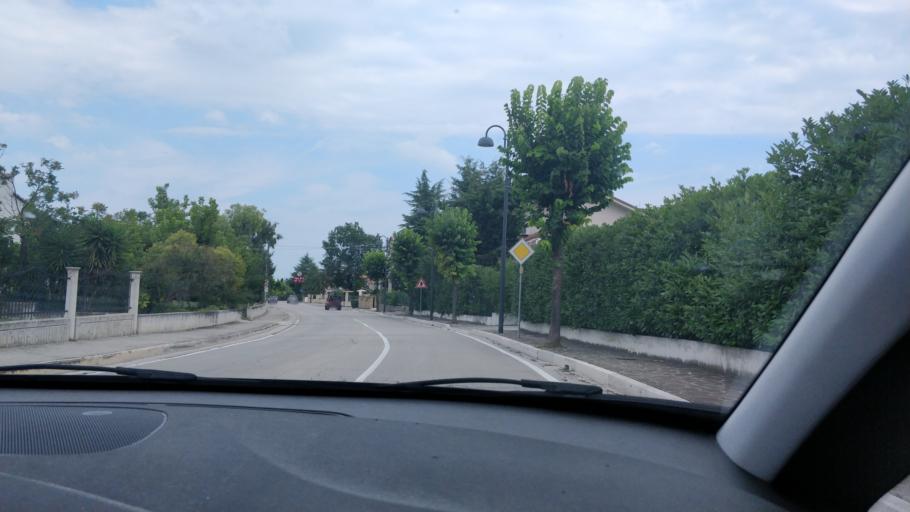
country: IT
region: Abruzzo
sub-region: Provincia di Chieti
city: San Vito Chietino
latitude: 42.2899
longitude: 14.4432
